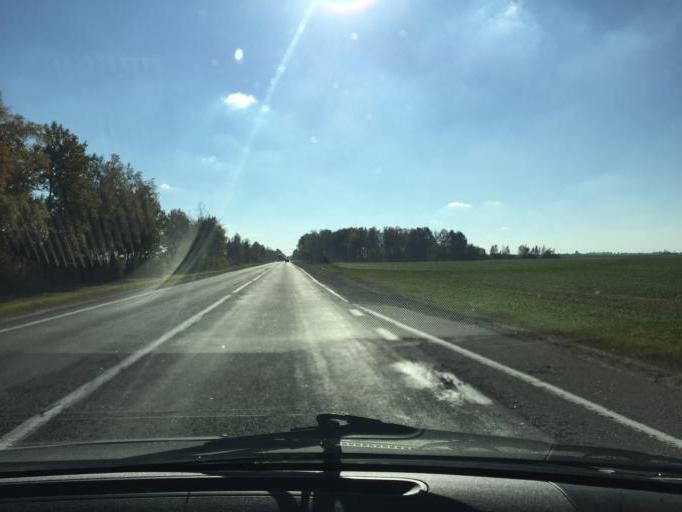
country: BY
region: Minsk
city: Salihorsk
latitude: 52.9120
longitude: 27.4800
